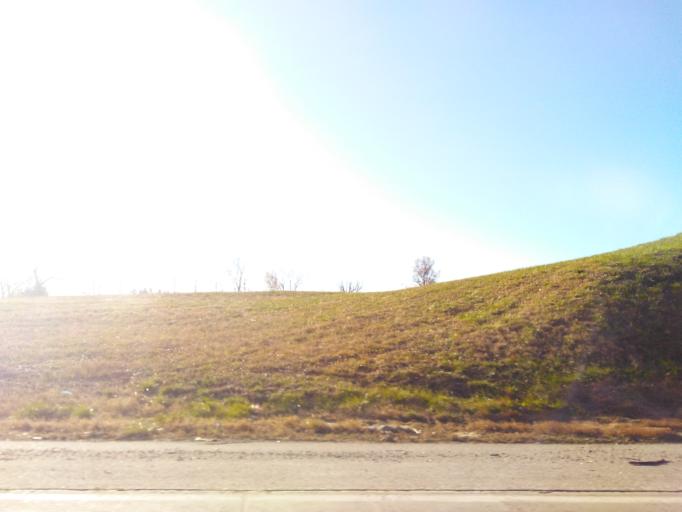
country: US
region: Illinois
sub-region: Madison County
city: Maryville
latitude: 38.7081
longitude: -89.9585
